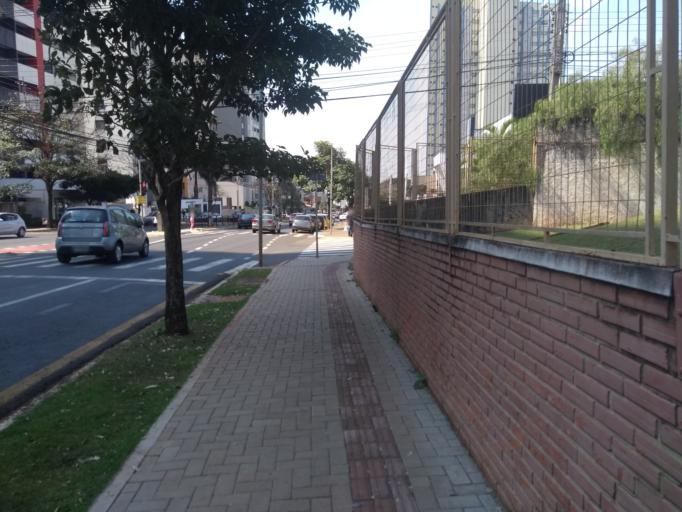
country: BR
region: Parana
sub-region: Londrina
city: Londrina
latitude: -23.3349
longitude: -51.1748
